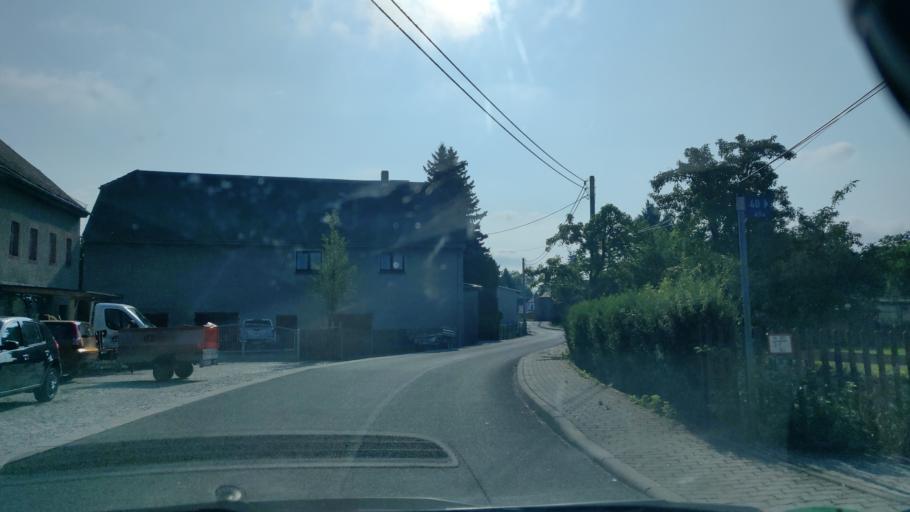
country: DE
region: Saxony
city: Konigsfeld
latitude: 51.0898
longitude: 12.7313
